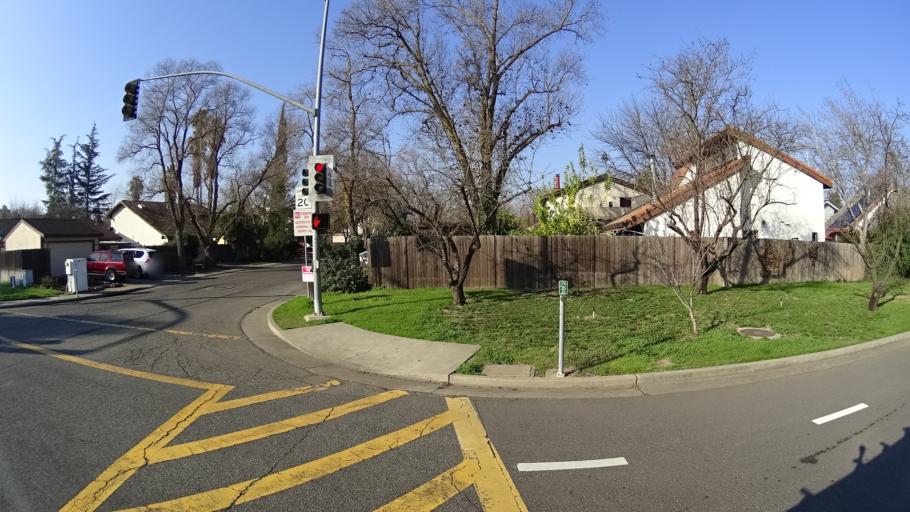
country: US
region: California
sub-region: Yolo County
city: Davis
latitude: 38.5507
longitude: -121.7792
